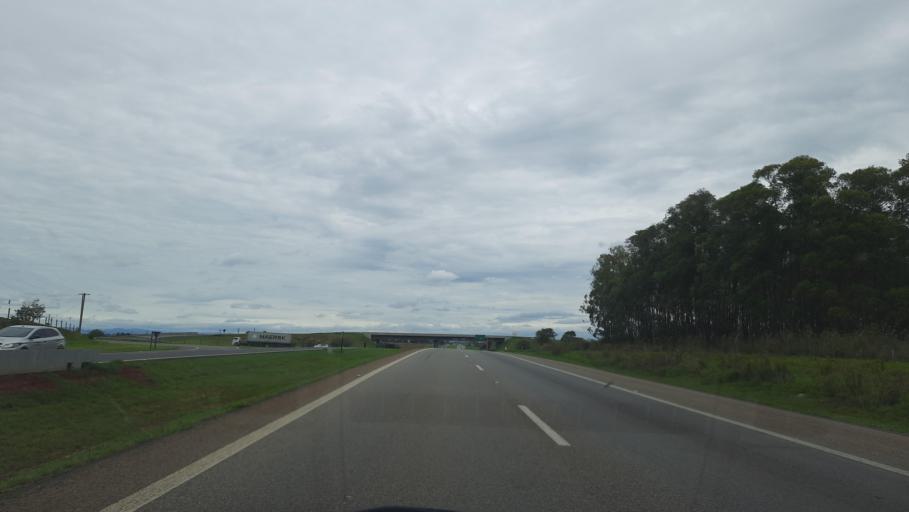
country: BR
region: Sao Paulo
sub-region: Moji-Guacu
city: Mogi-Gaucu
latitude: -22.2913
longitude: -46.9706
